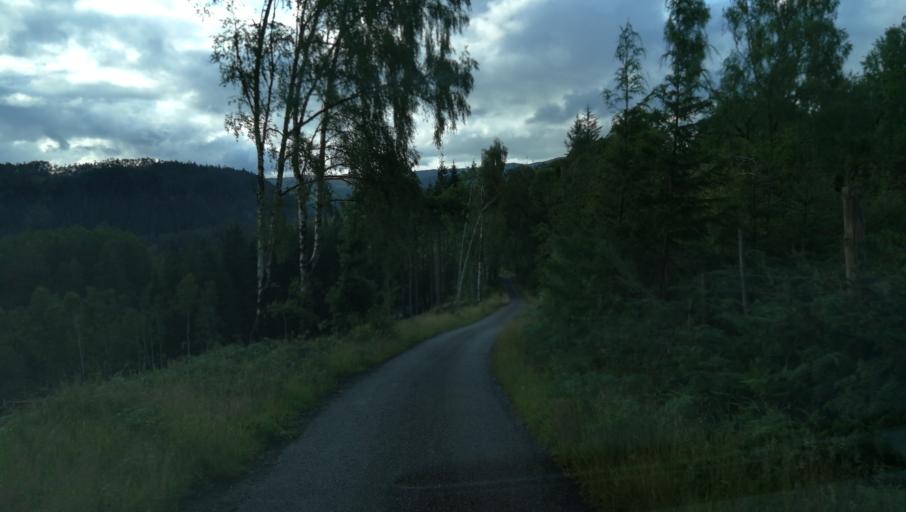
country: GB
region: Scotland
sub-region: Highland
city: Spean Bridge
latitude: 57.0703
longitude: -4.8286
